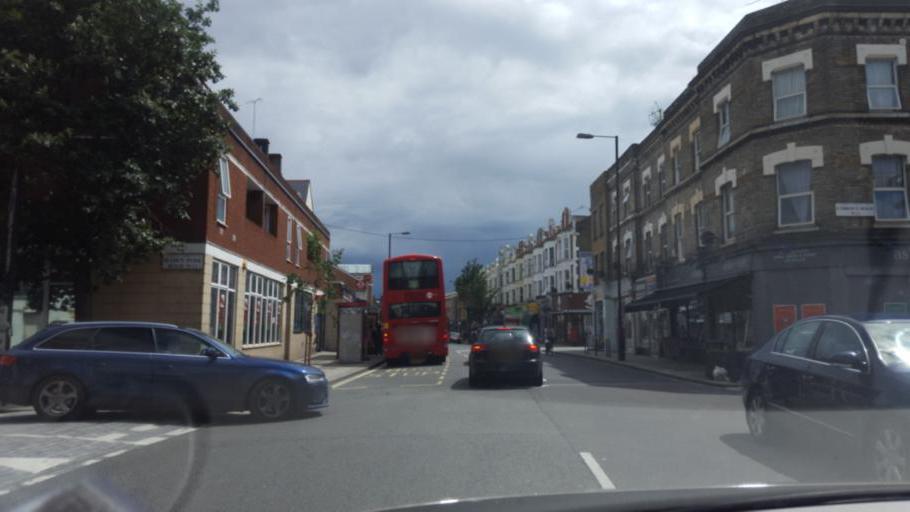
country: GB
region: England
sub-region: Greater London
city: Hammersmith
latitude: 51.5039
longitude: -0.2436
